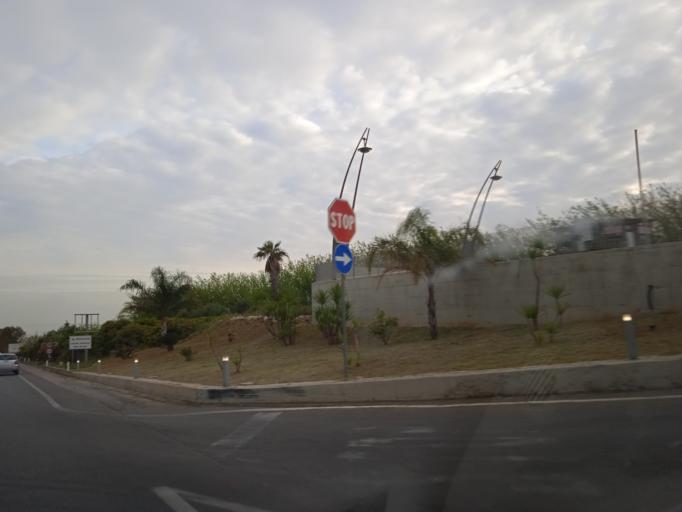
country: IT
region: Sicily
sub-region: Palermo
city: Portella di Mare
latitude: 38.0653
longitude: 13.4611
